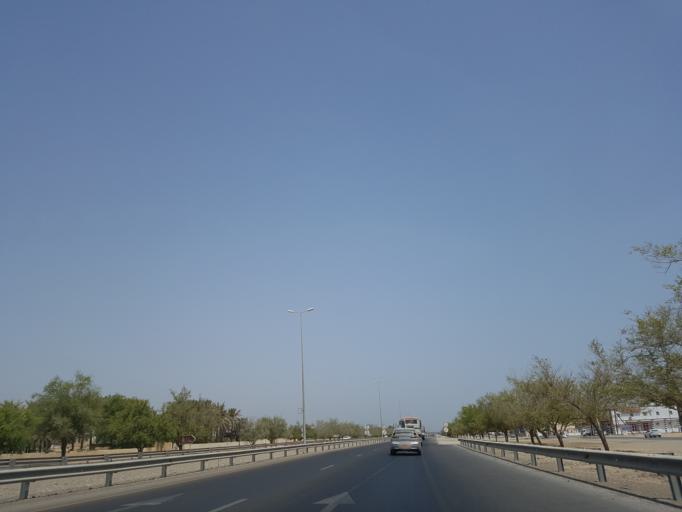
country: OM
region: Al Batinah
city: Saham
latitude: 24.1570
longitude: 56.8657
